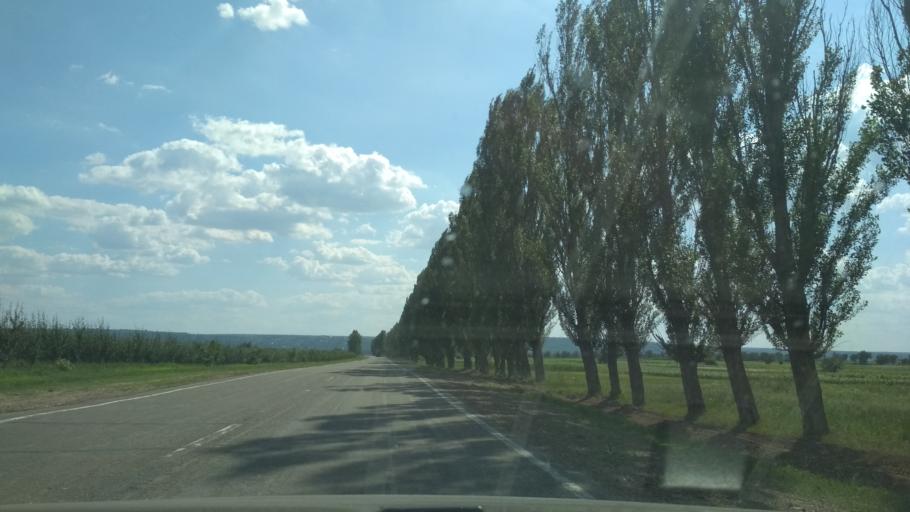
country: MD
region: Chisinau
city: Vadul lui Voda
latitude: 47.1284
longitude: 29.1225
